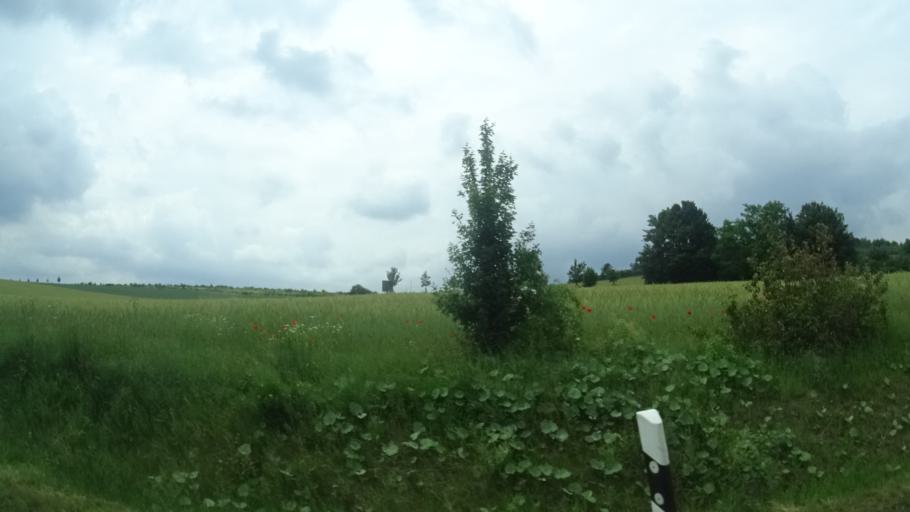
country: DE
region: Hesse
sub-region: Regierungsbezirk Kassel
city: Fulda
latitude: 50.5409
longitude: 9.6188
